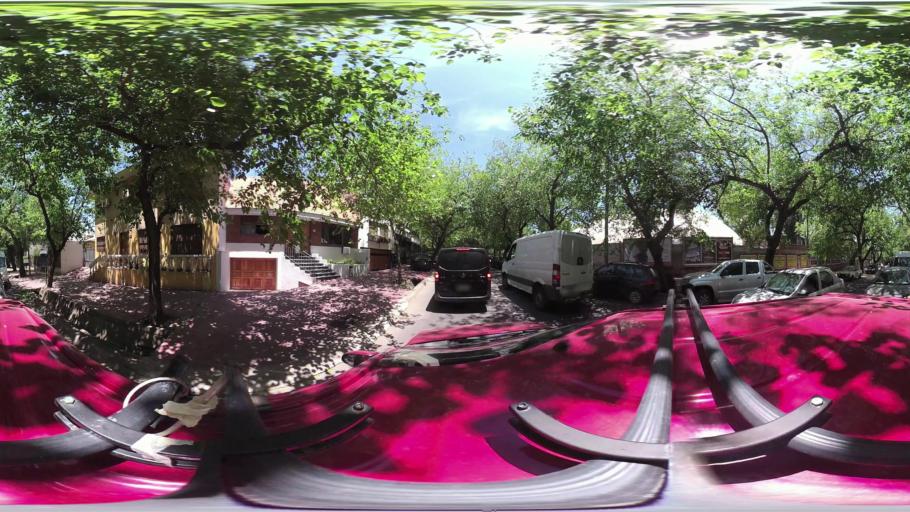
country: AR
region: Mendoza
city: Mendoza
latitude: -32.8995
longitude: -68.8538
